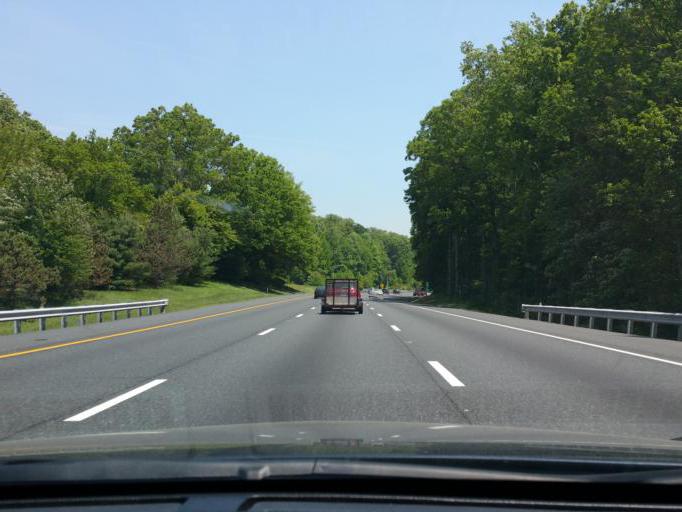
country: US
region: Maryland
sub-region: Harford County
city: Riverside
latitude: 39.4989
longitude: -76.2282
